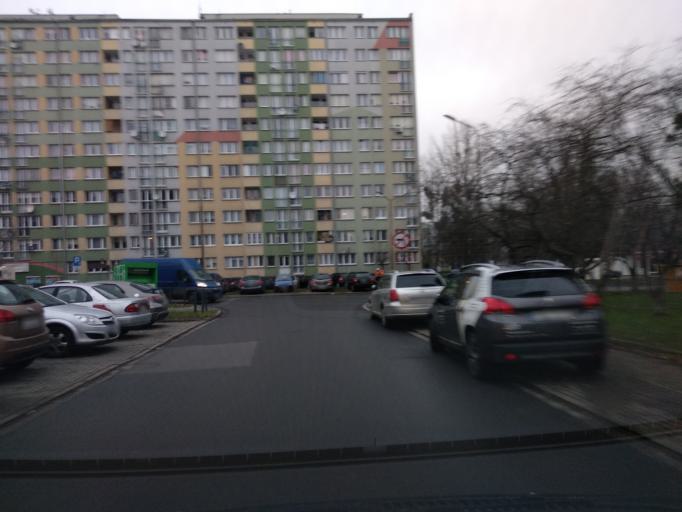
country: PL
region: Lower Silesian Voivodeship
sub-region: Powiat wroclawski
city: Wroclaw
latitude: 51.0843
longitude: 17.0406
